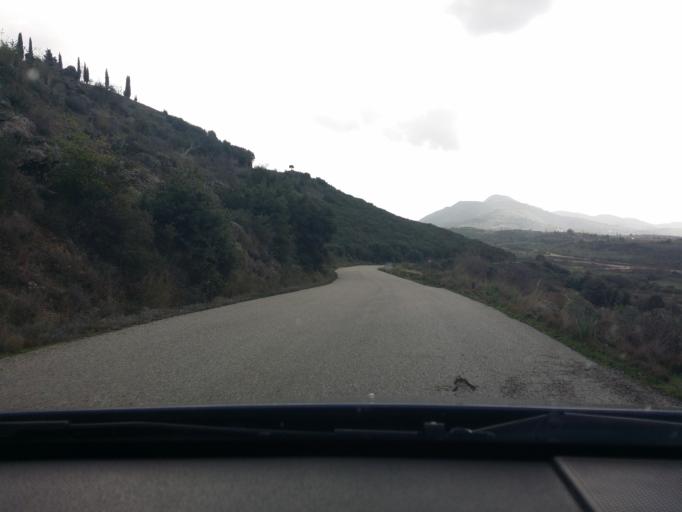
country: GR
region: West Greece
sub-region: Nomos Aitolias kai Akarnanias
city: Fitiai
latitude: 38.6929
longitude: 21.1775
